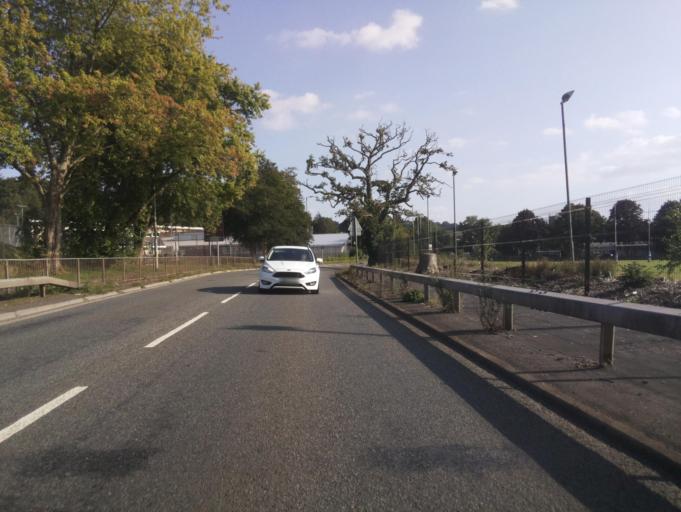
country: GB
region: England
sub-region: Devon
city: Tiverton
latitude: 50.9112
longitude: -3.4898
